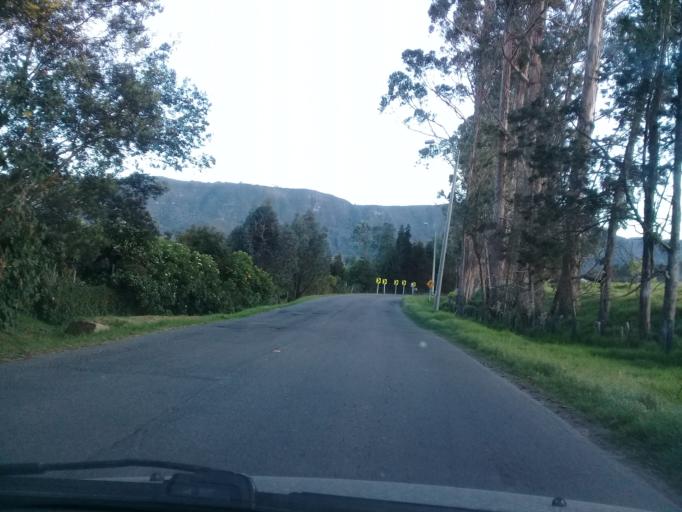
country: CO
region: Cundinamarca
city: Tenjo
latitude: 4.8525
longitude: -74.1336
